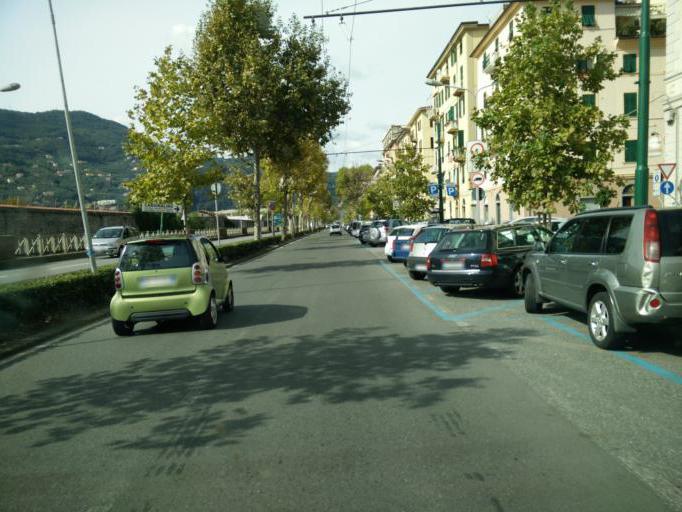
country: IT
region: Liguria
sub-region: Provincia di La Spezia
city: La Spezia
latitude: 44.1024
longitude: 9.8196
